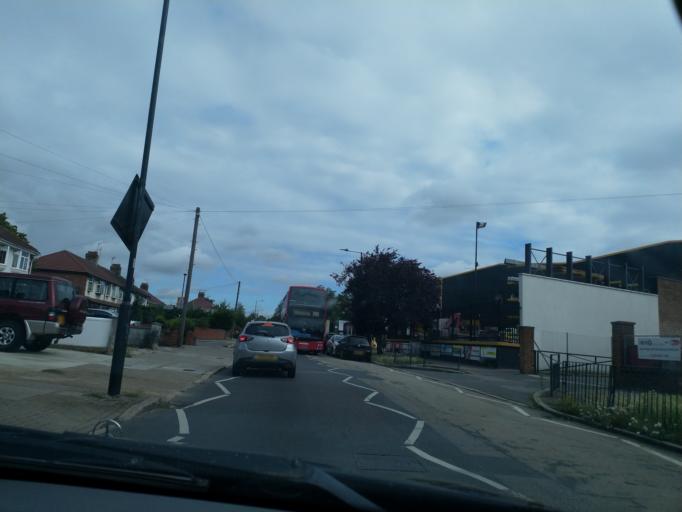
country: GB
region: England
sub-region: Greater London
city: Wembley
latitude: 51.5373
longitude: -0.3058
